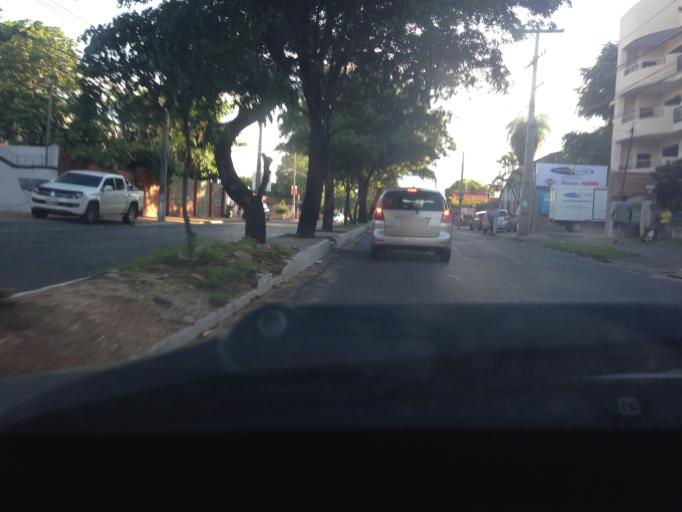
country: PY
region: Central
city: Lambare
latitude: -25.3175
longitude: -57.5911
